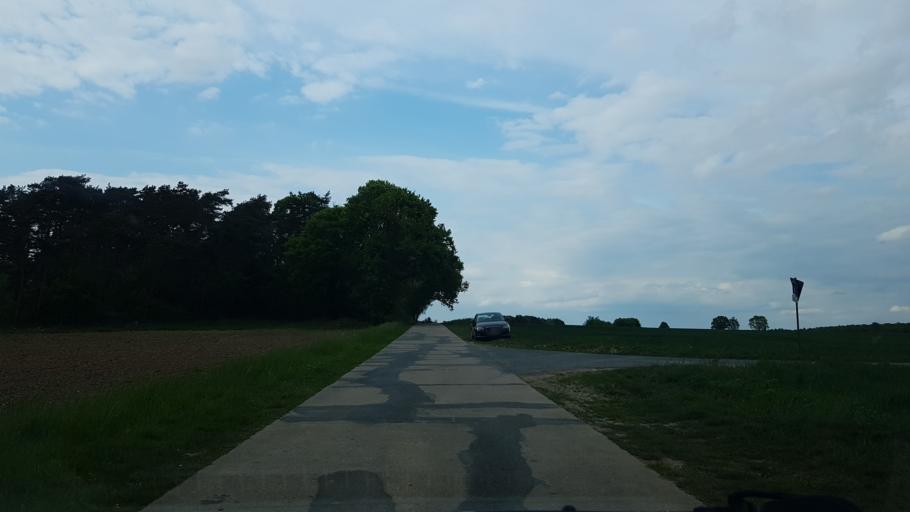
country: DE
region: Lower Saxony
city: Vastorf
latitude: 53.1797
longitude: 10.5513
